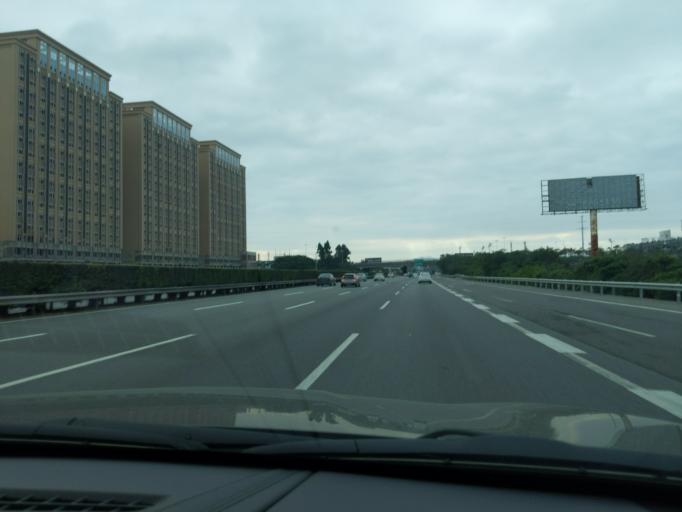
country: CN
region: Fujian
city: Neikeng
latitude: 24.7833
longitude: 118.4708
